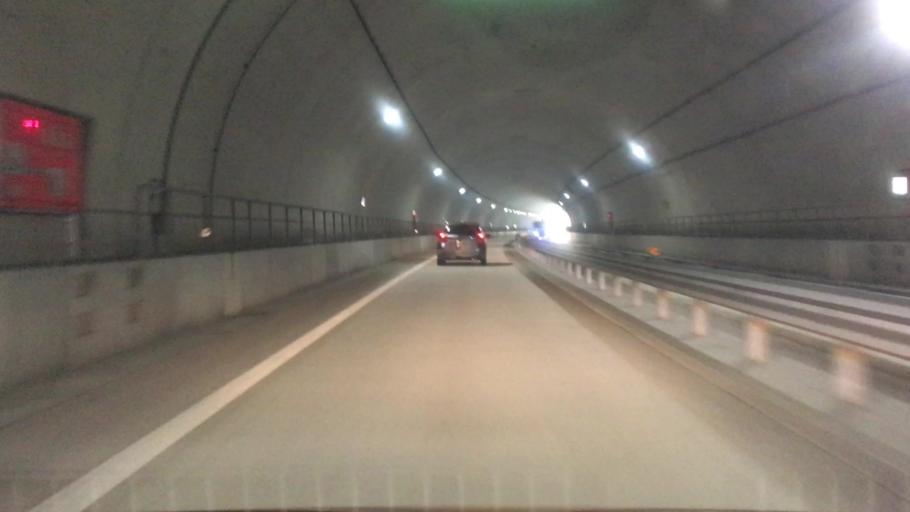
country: JP
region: Tottori
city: Tottori
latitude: 35.5737
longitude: 134.3183
